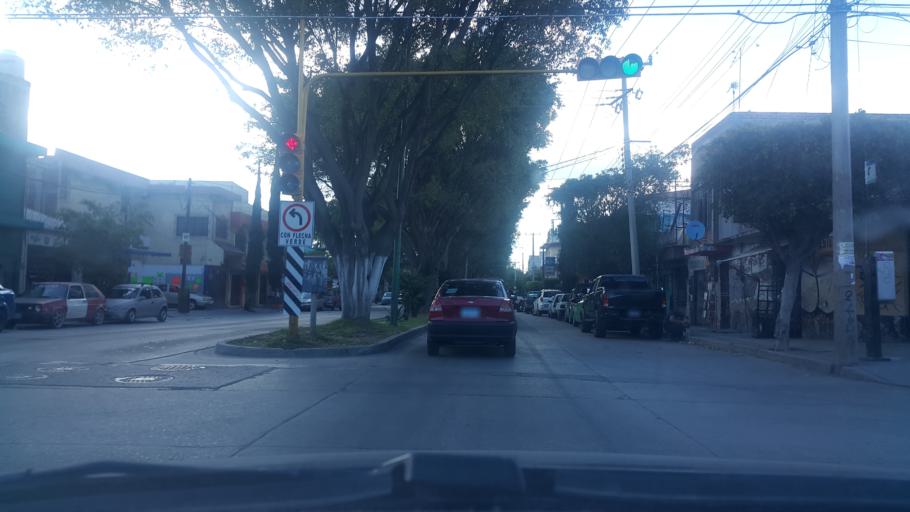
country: MX
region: Guanajuato
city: Leon
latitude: 21.1327
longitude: -101.6500
